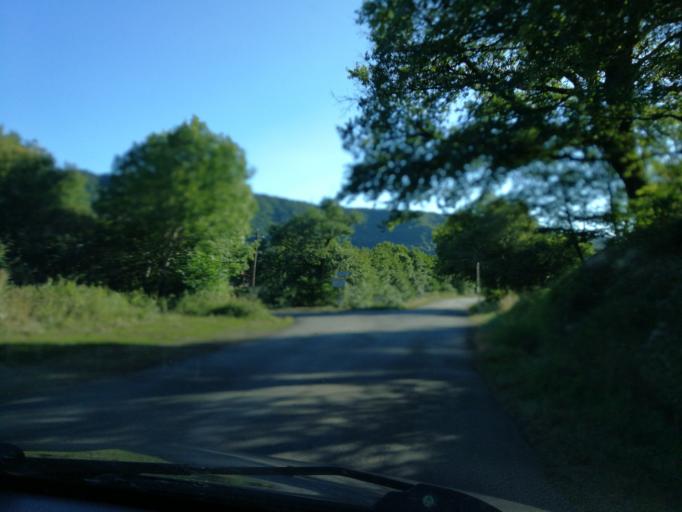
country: FR
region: Auvergne
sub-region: Departement du Cantal
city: Saint-Cernin
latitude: 45.1276
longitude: 2.4937
